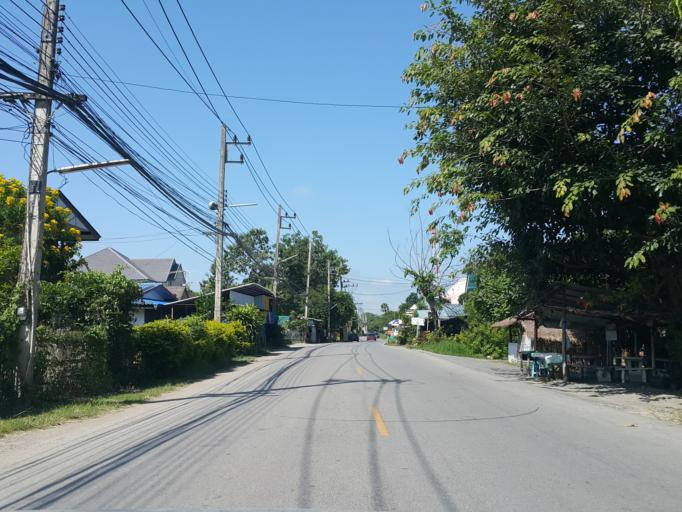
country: TH
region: Chiang Mai
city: San Kamphaeng
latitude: 18.7398
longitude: 99.1547
